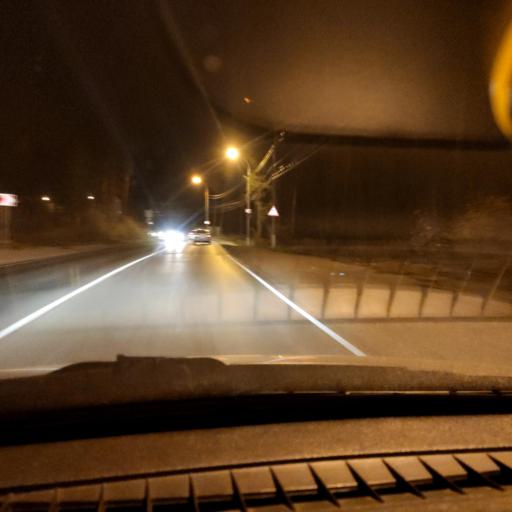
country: RU
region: Samara
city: Tol'yatti
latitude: 53.4869
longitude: 49.3113
